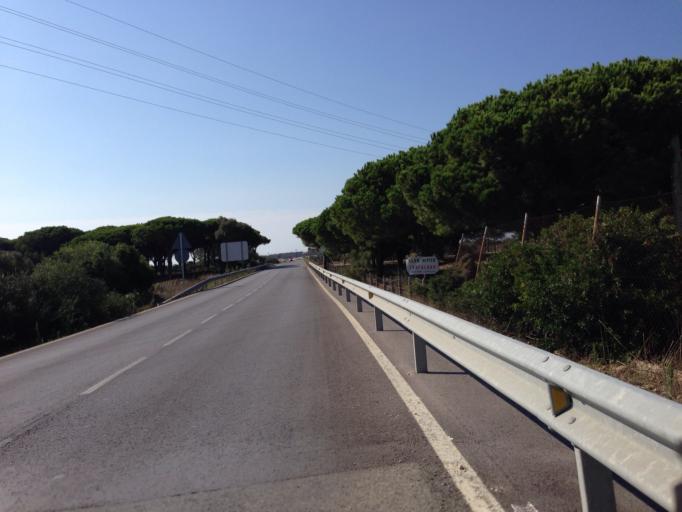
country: ES
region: Andalusia
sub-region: Provincia de Cadiz
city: Vejer de la Frontera
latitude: 36.1958
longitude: -6.0310
